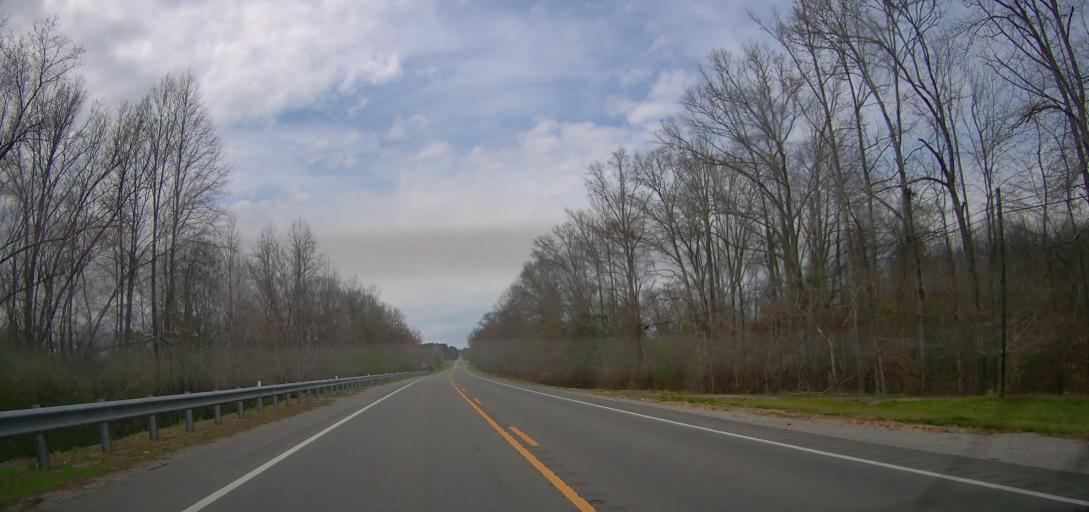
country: US
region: Alabama
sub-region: Marion County
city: Guin
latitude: 33.9974
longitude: -87.9303
